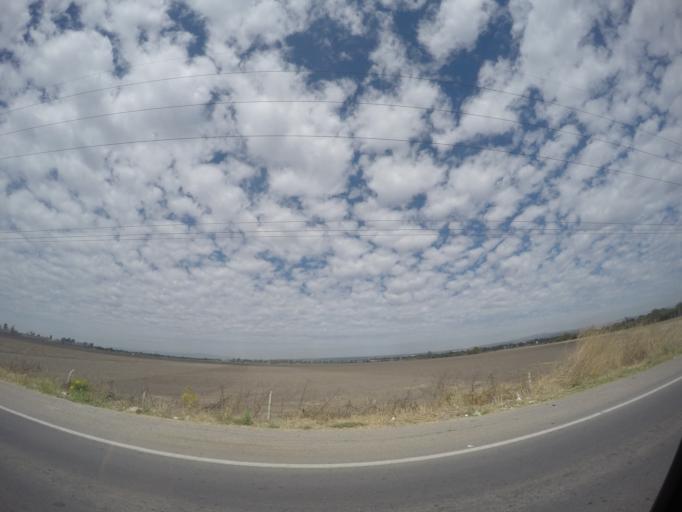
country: MX
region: Guanajuato
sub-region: Leon
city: San Antonio de los Tepetates
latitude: 21.0426
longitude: -101.6918
